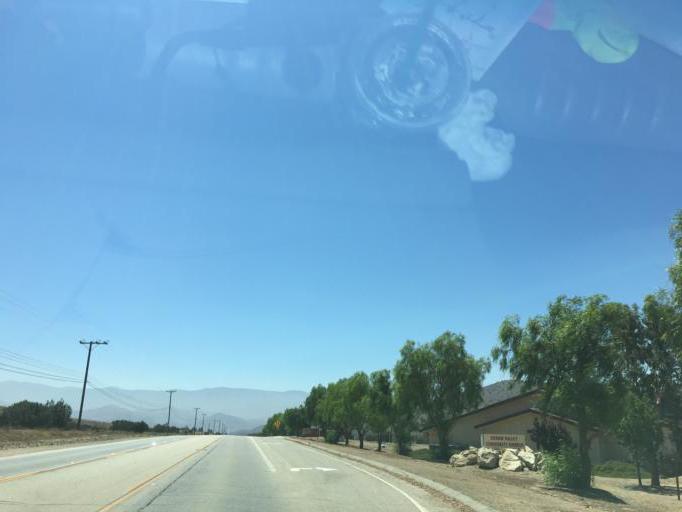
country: US
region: California
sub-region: Los Angeles County
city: Acton
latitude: 34.5102
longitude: -118.2348
